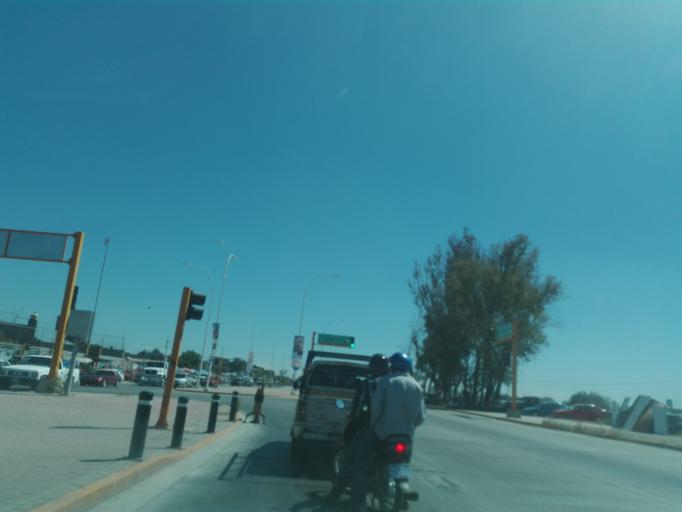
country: MX
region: Guanajuato
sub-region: Leon
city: San Jose de Duran (Los Troncoso)
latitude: 21.0678
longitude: -101.6372
